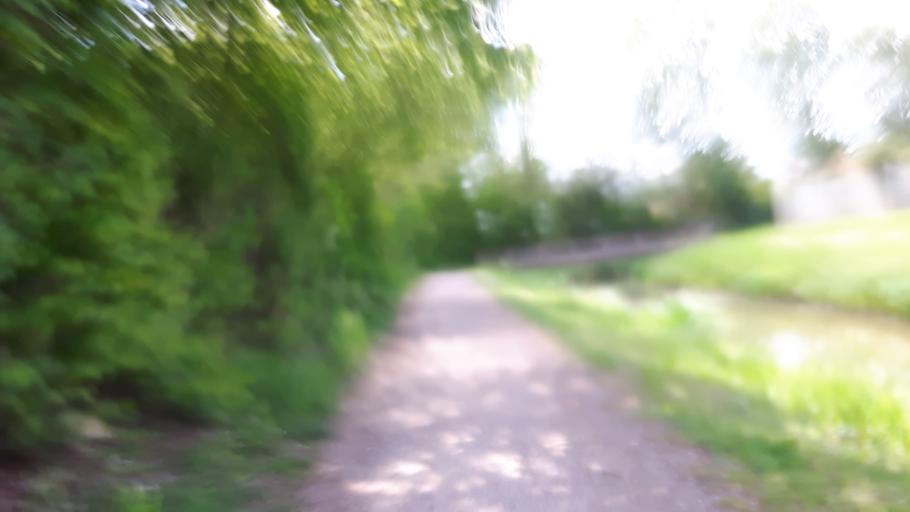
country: DE
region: Bremen
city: Bremen
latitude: 53.0385
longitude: 8.8599
